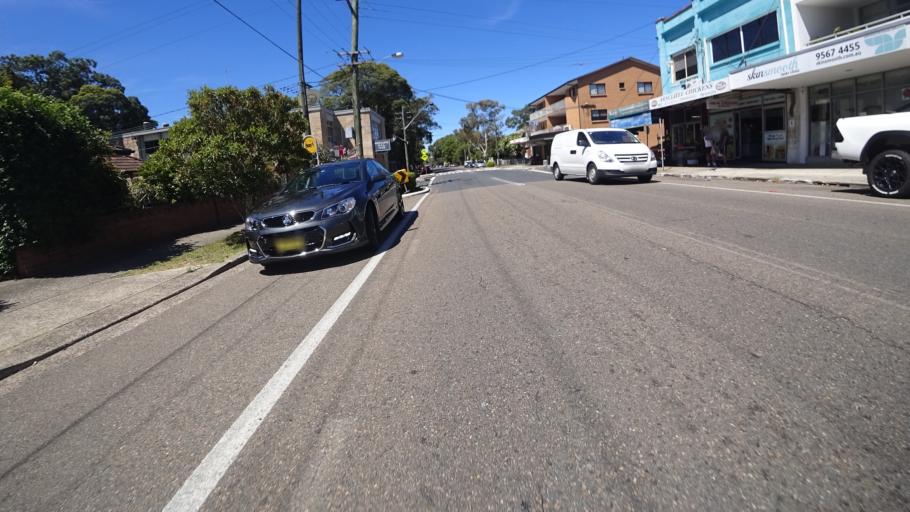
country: AU
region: New South Wales
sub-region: Rockdale
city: Bardwell Valley
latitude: -33.9367
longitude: 151.1418
